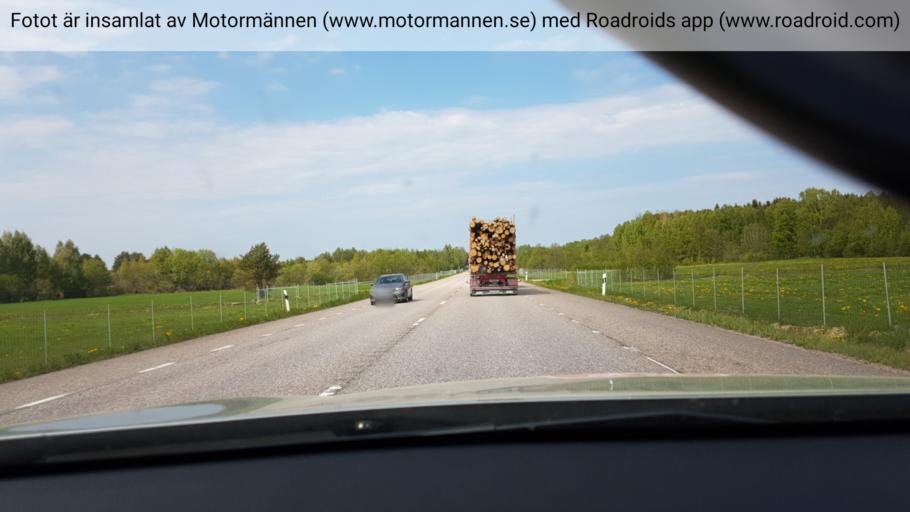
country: SE
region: Uppsala
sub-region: Alvkarleby Kommun
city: AElvkarleby
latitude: 60.5762
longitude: 17.4662
